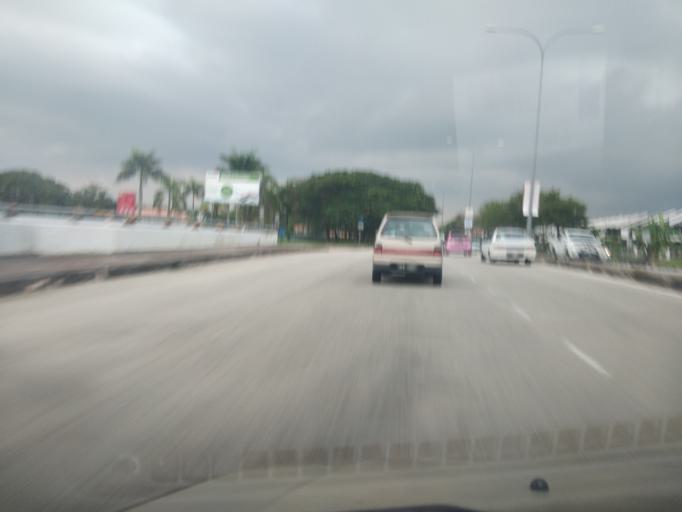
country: MY
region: Penang
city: Kepala Batas
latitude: 5.5195
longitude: 100.4709
